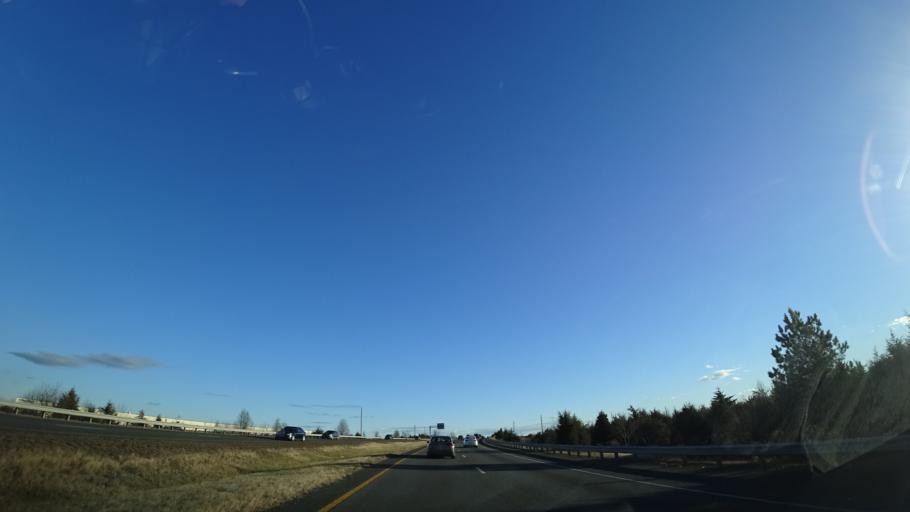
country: US
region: Virginia
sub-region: Prince William County
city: Bull Run
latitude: 38.7889
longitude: -77.5519
